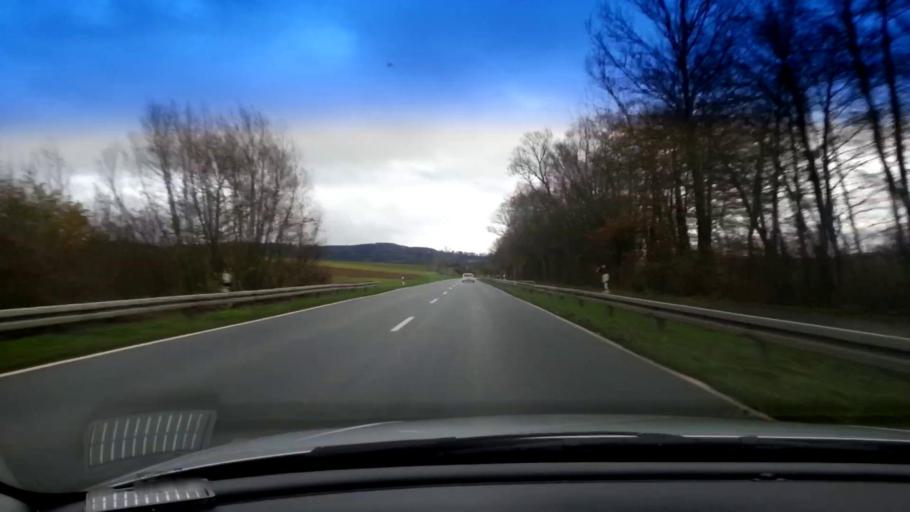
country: DE
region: Bavaria
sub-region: Upper Franconia
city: Ebensfeld
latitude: 50.0428
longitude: 10.9969
